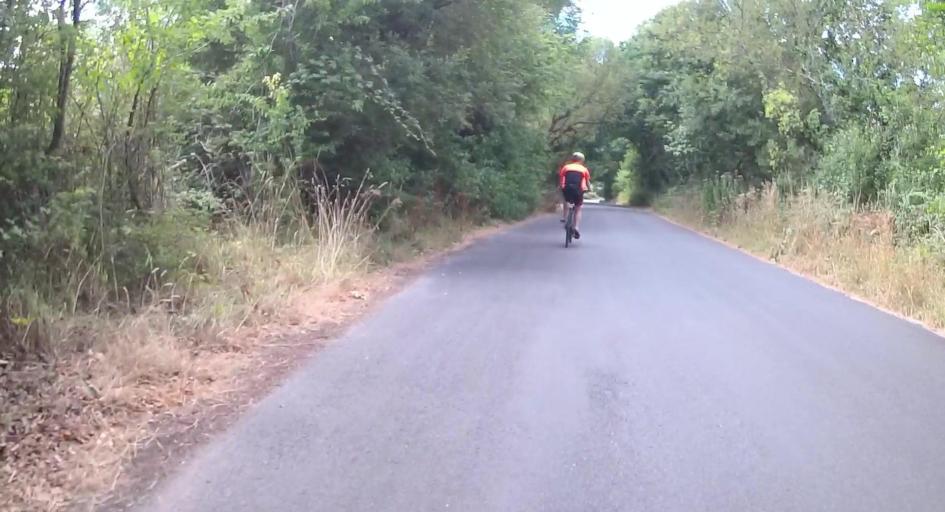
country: GB
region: England
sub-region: Dorset
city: Wareham
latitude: 50.6736
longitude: -2.1001
